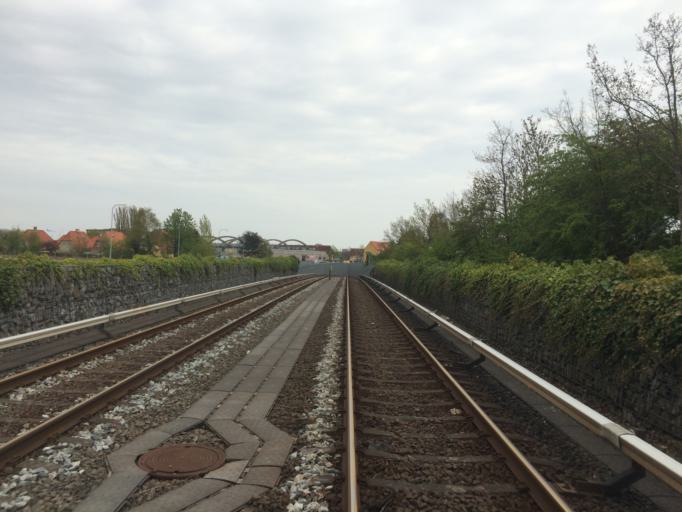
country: DK
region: Capital Region
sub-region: Tarnby Kommune
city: Tarnby
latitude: 55.6413
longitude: 12.6419
